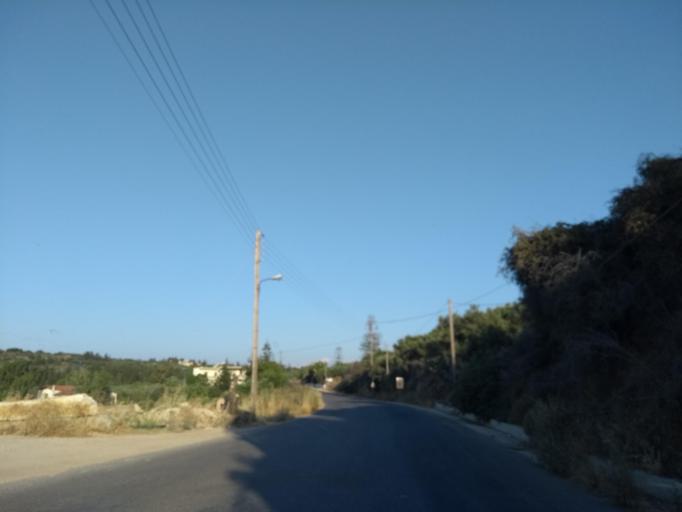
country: GR
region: Crete
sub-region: Nomos Chanias
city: Kalivai
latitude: 35.4187
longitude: 24.1888
